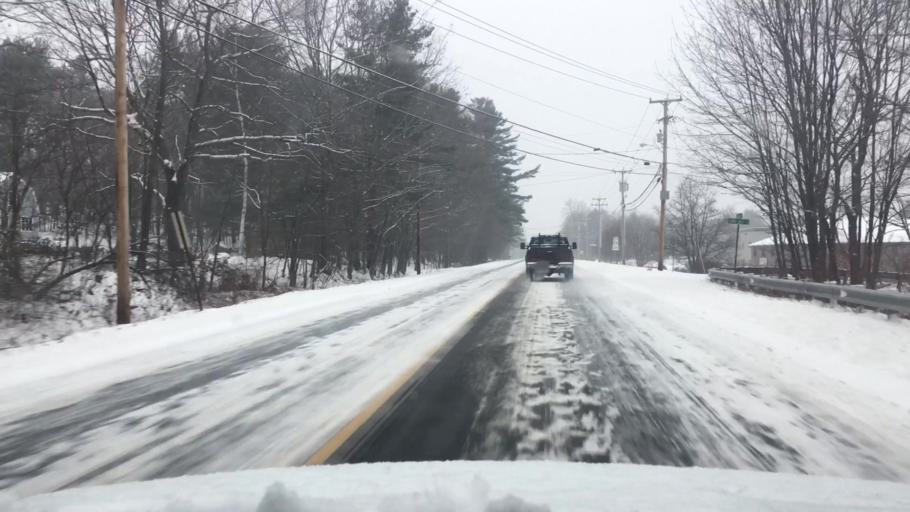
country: US
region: Maine
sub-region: Cumberland County
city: Cumberland Center
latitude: 43.8591
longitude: -70.3220
